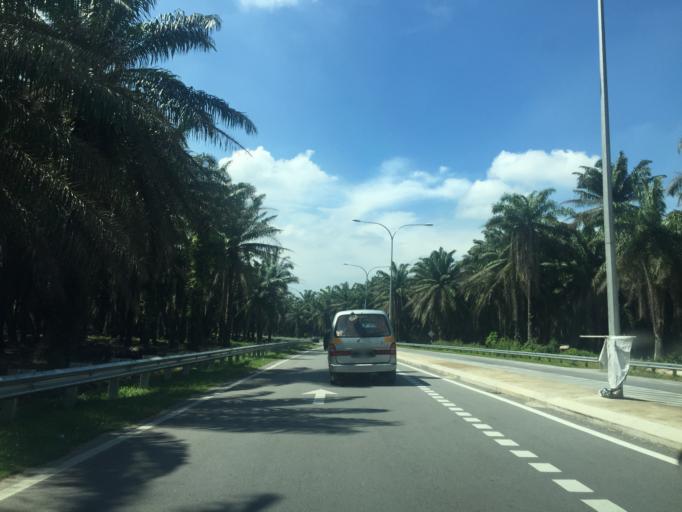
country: MY
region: Penang
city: Tasek Glugor
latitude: 5.5114
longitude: 100.5316
